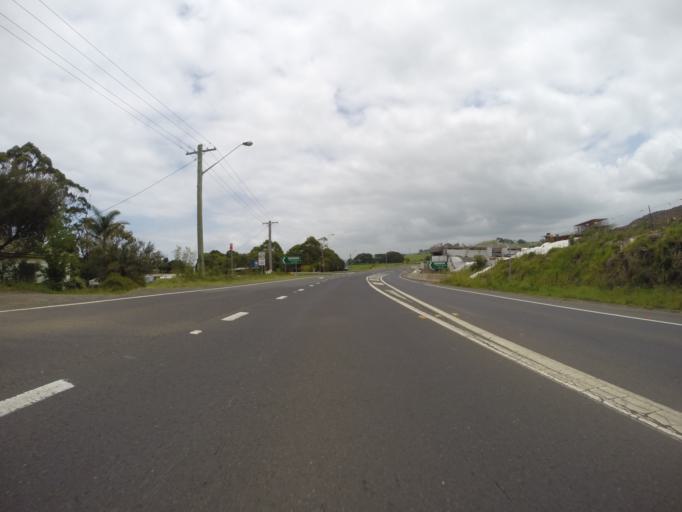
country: AU
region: New South Wales
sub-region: Kiama
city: Gerringong
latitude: -34.7439
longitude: 150.8177
